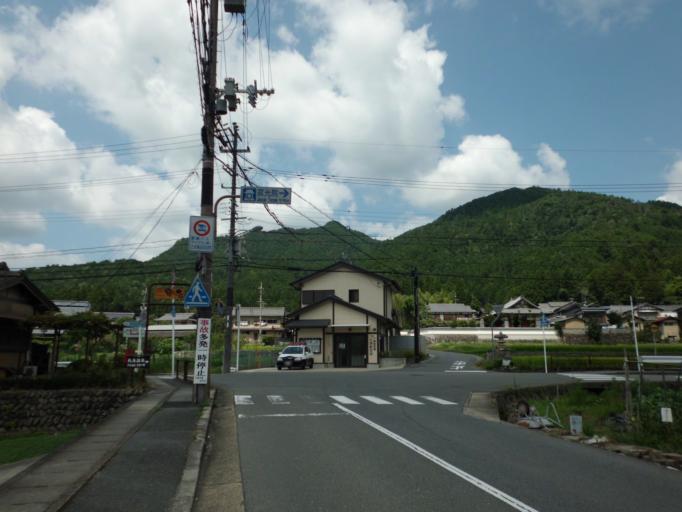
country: JP
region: Shiga Prefecture
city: Kitahama
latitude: 35.1127
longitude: 135.8259
